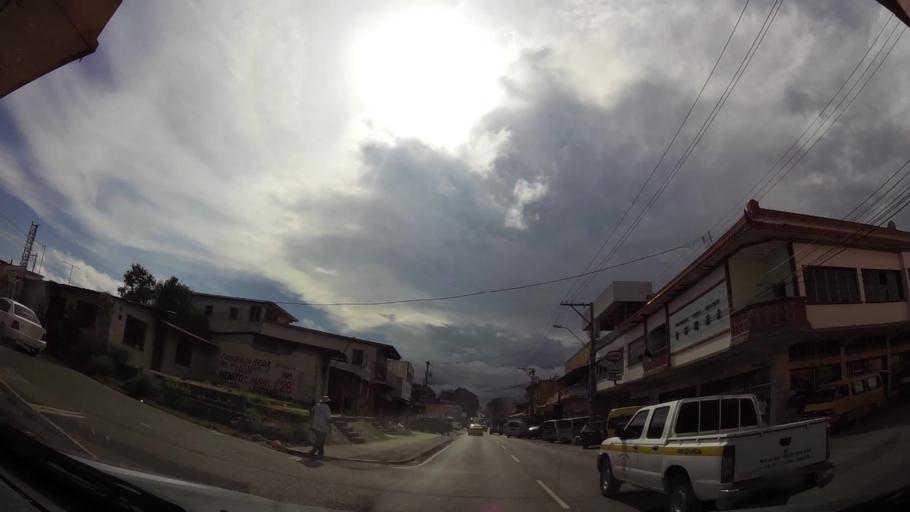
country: PA
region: Panama
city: La Chorrera
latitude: 8.8774
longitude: -79.7851
